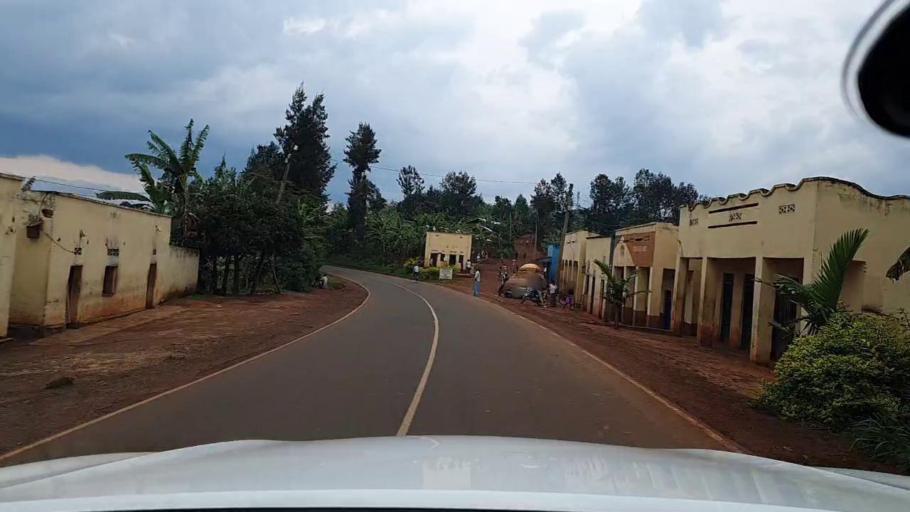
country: RW
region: Western Province
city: Cyangugu
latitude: -2.6456
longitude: 28.9581
